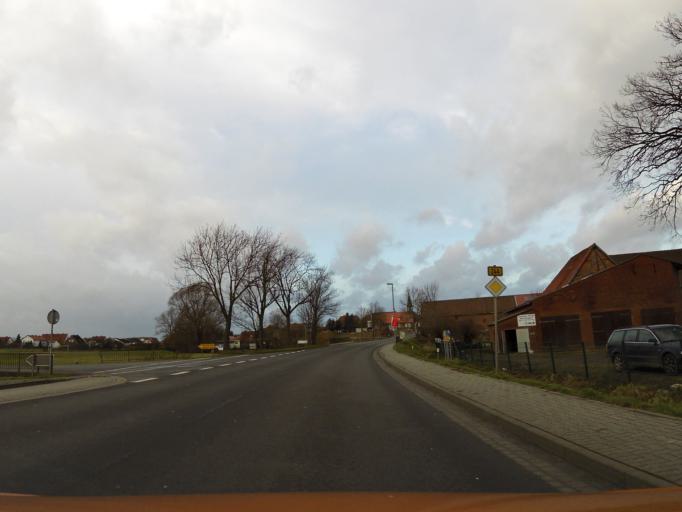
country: DE
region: Lower Saxony
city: Querenhorst
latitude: 52.3344
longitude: 10.9644
